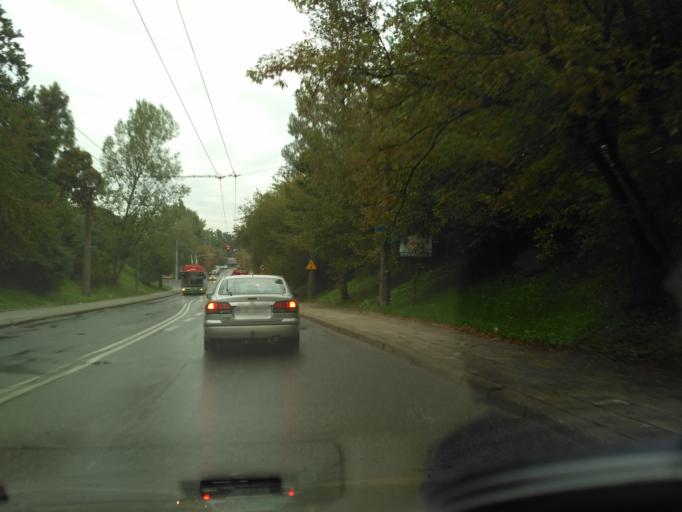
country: PL
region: Lublin Voivodeship
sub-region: Powiat lubelski
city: Lublin
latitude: 51.2472
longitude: 22.6028
